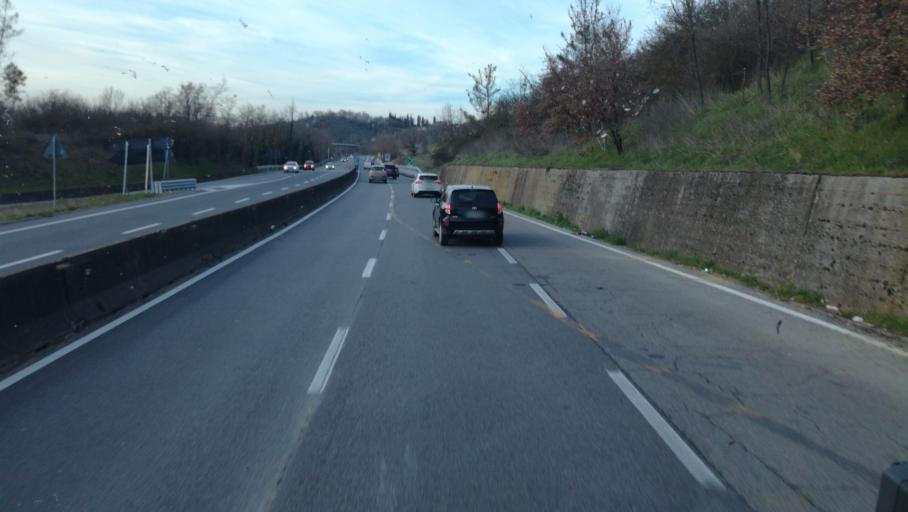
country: IT
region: Tuscany
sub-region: Provincia di Siena
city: Belverde
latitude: 43.3567
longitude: 11.3050
